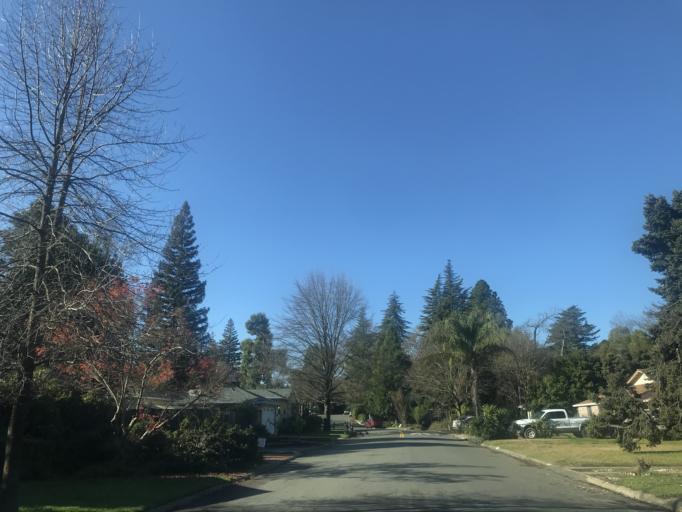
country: US
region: California
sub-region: Sacramento County
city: Sacramento
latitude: 38.5312
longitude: -121.5025
